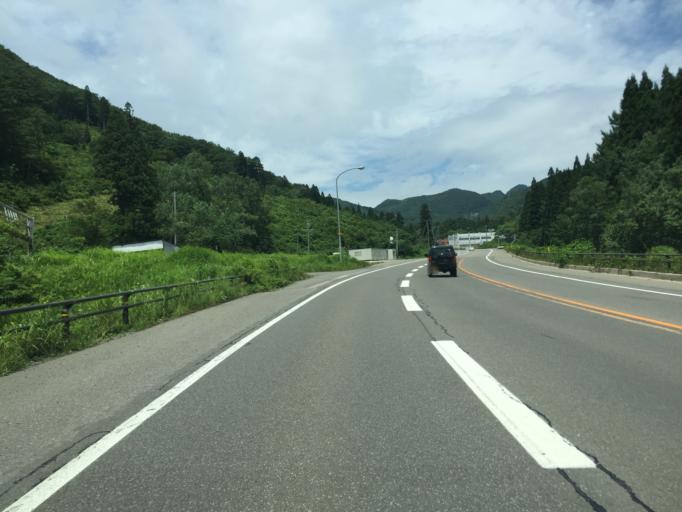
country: JP
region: Yamagata
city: Yonezawa
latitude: 37.8203
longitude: 140.2731
